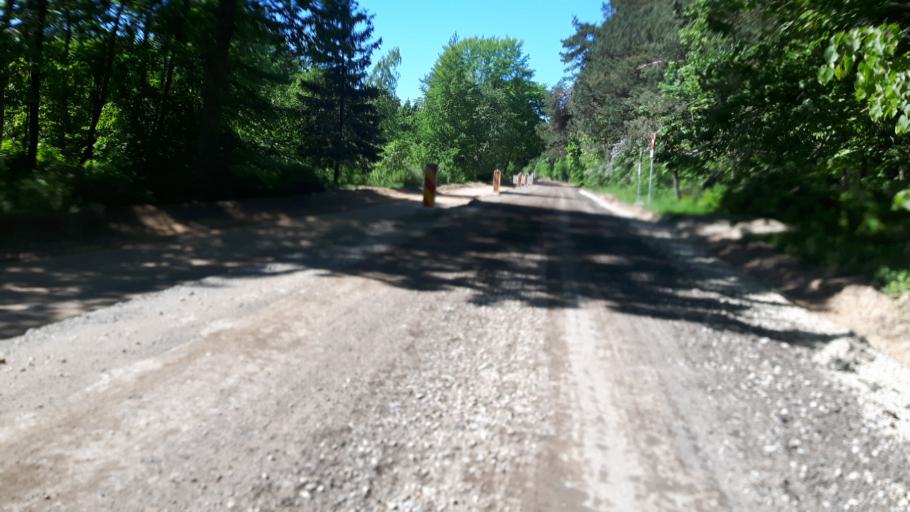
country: EE
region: Ida-Virumaa
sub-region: Narva-Joesuu linn
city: Narva-Joesuu
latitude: 59.4175
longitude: 27.9690
